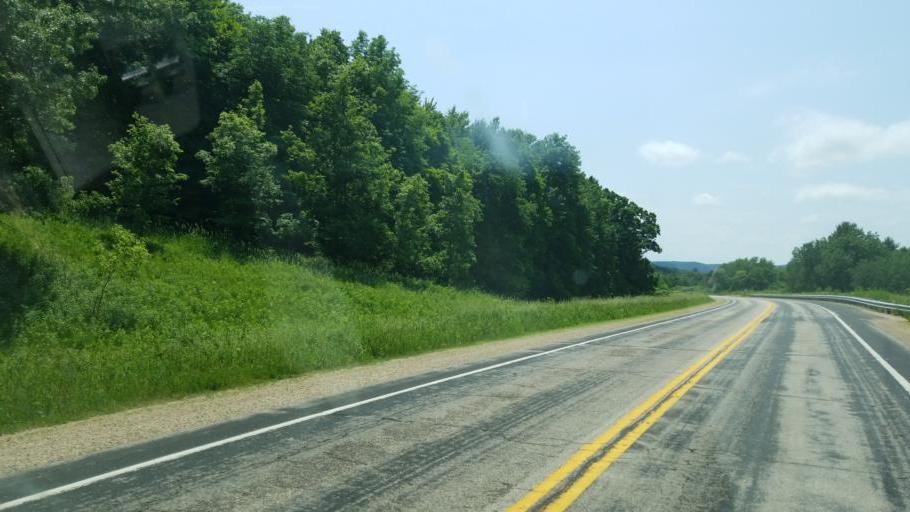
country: US
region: Wisconsin
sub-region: Monroe County
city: Cashton
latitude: 43.6243
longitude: -90.6058
